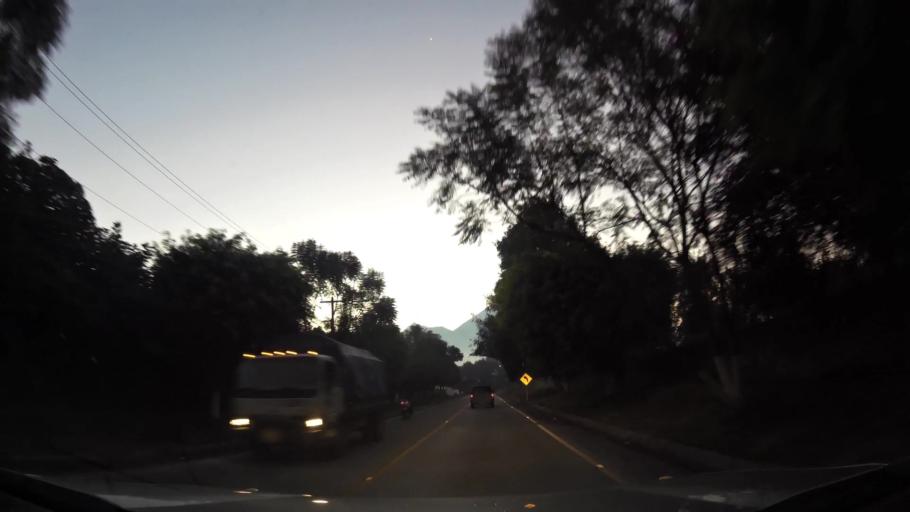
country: GT
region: Sacatepequez
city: Ciudad Vieja
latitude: 14.5301
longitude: -90.7557
